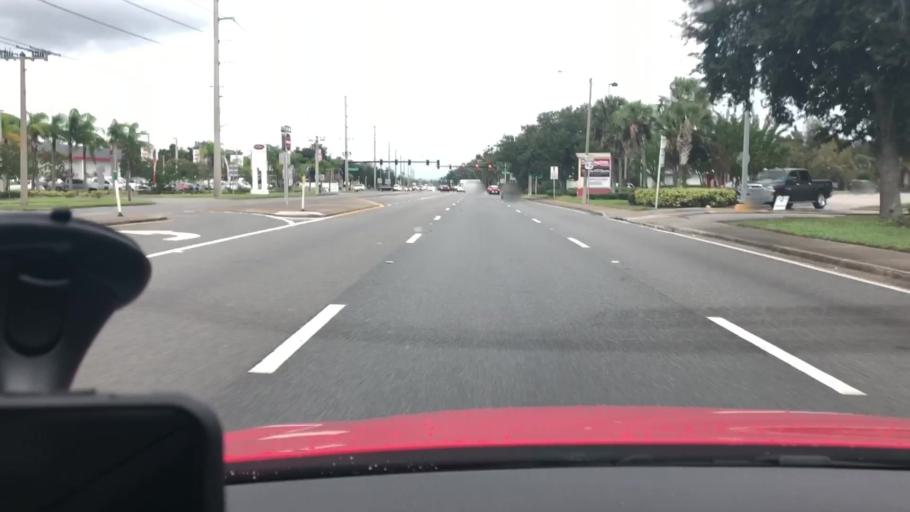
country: US
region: Florida
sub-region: Volusia County
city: Daytona Beach
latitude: 29.2051
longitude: -81.0408
